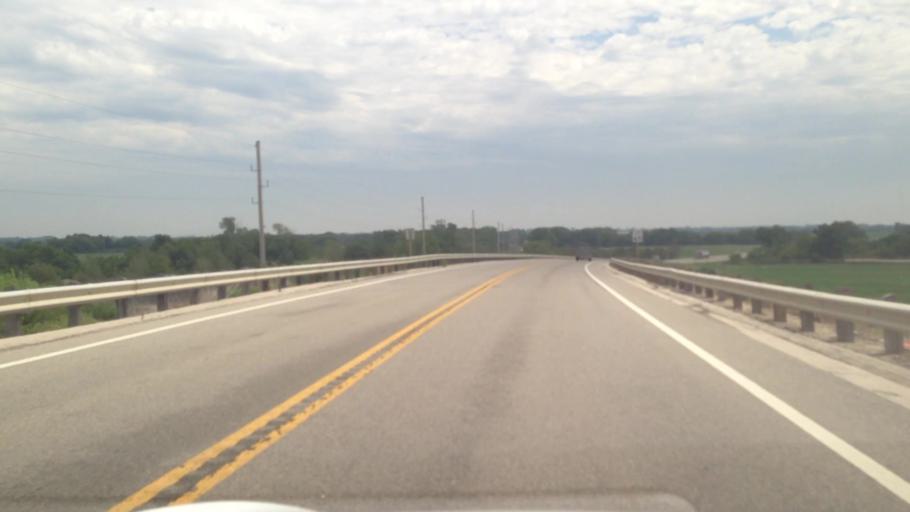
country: US
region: Kansas
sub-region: Allen County
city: Iola
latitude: 37.9216
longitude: -95.1644
